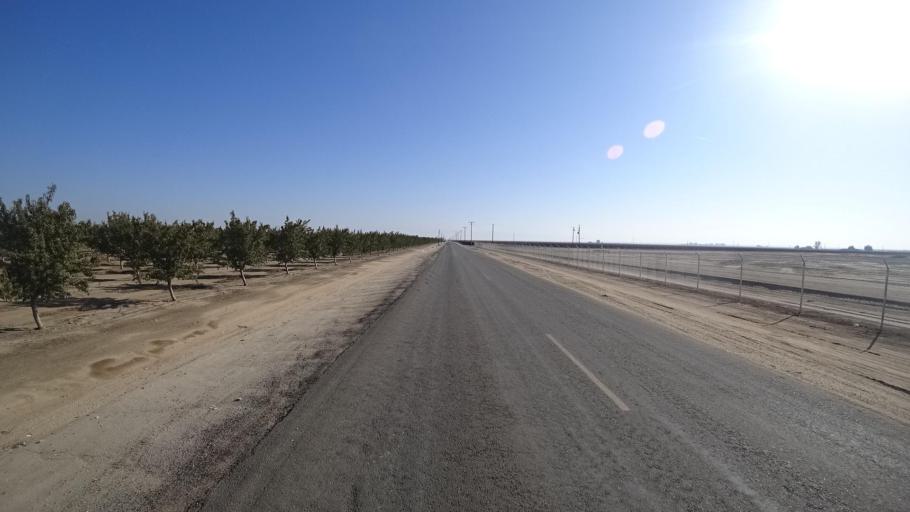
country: US
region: California
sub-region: Kern County
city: Delano
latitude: 35.7687
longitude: -119.2118
